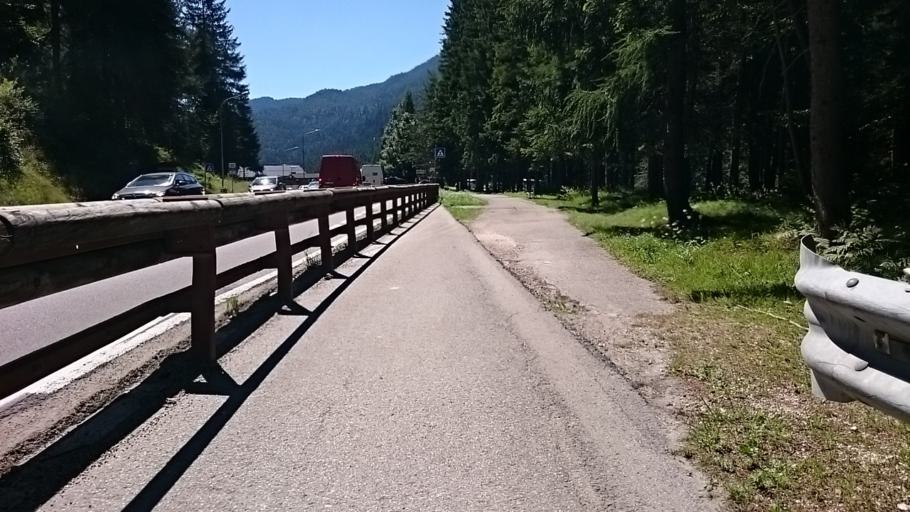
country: IT
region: Veneto
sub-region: Provincia di Belluno
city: Cortina d'Ampezzo
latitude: 46.5092
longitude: 12.1563
